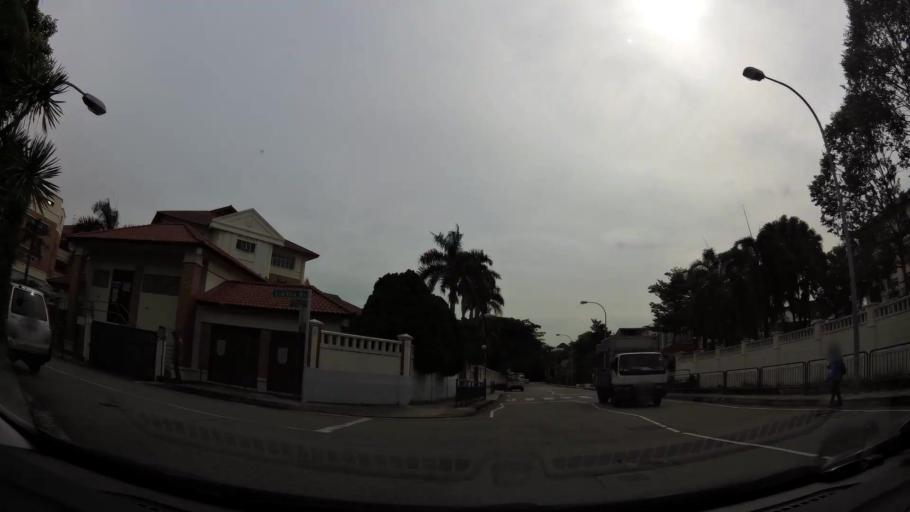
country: SG
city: Singapore
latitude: 1.3315
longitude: 103.8017
